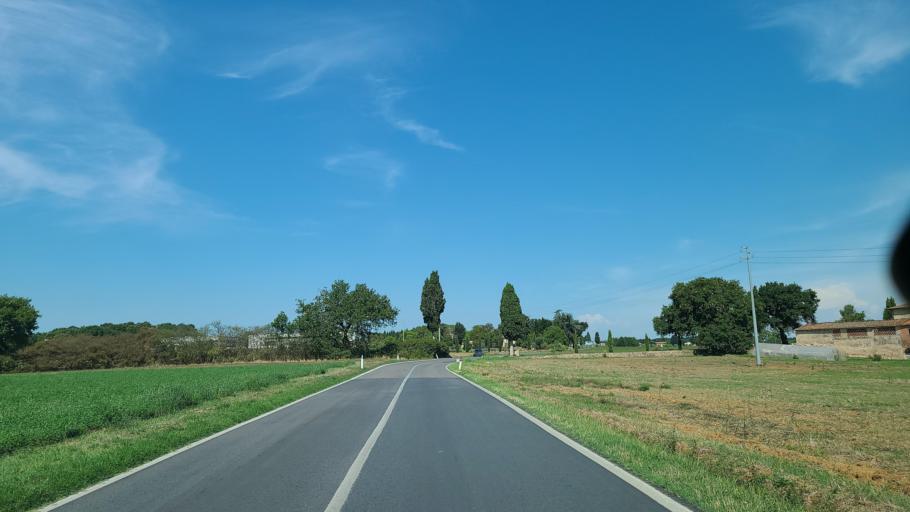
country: IT
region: Tuscany
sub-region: Provincia di Siena
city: Staggia
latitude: 43.4028
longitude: 11.1717
